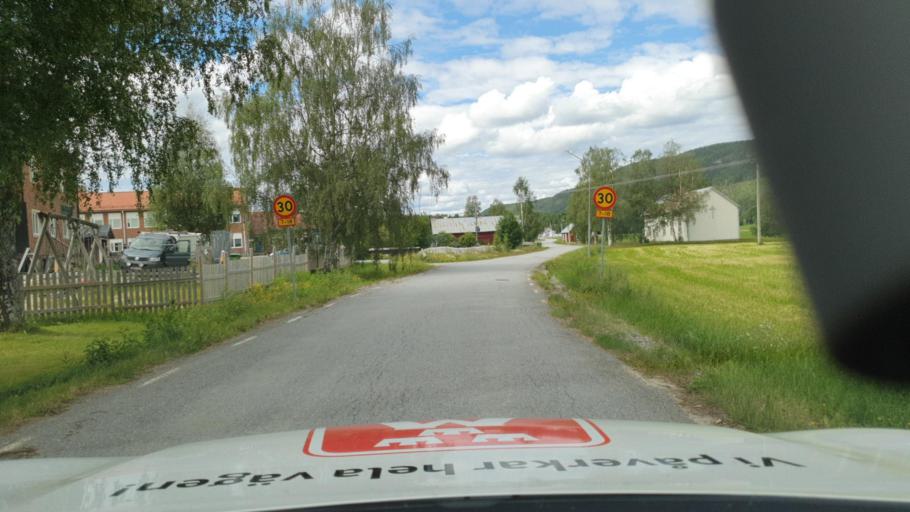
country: SE
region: Vaesterbotten
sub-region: Bjurholms Kommun
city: Bjurholm
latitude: 63.9212
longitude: 19.0615
